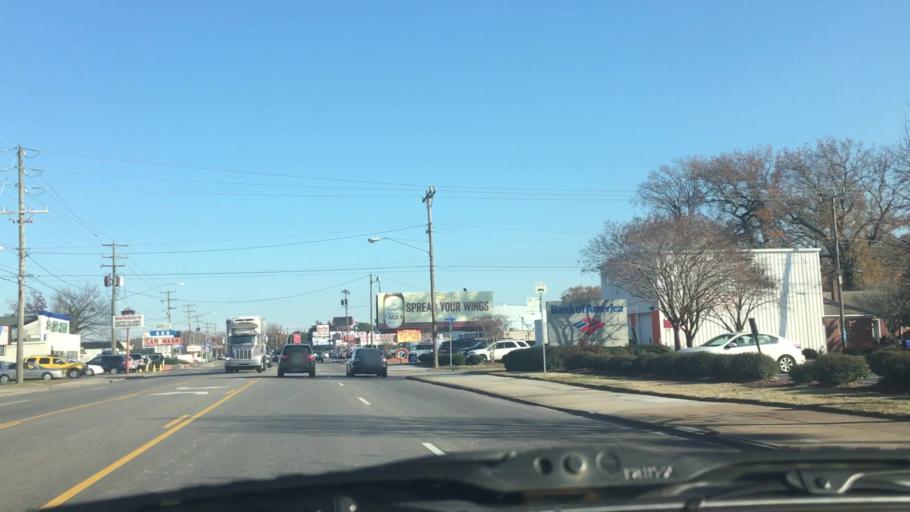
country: US
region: Virginia
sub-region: City of Norfolk
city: Norfolk
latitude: 36.9150
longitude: -76.2466
